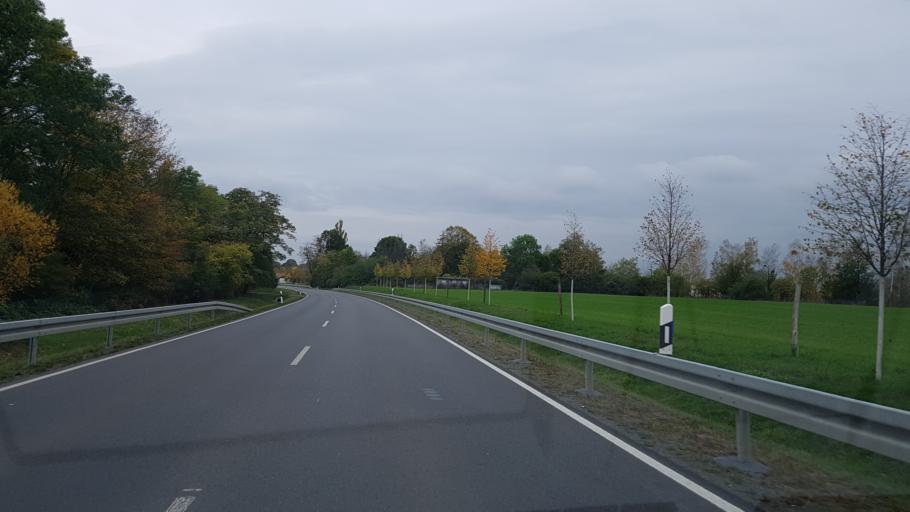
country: DE
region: Saxony
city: Wurzen
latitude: 51.3756
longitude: 12.7618
